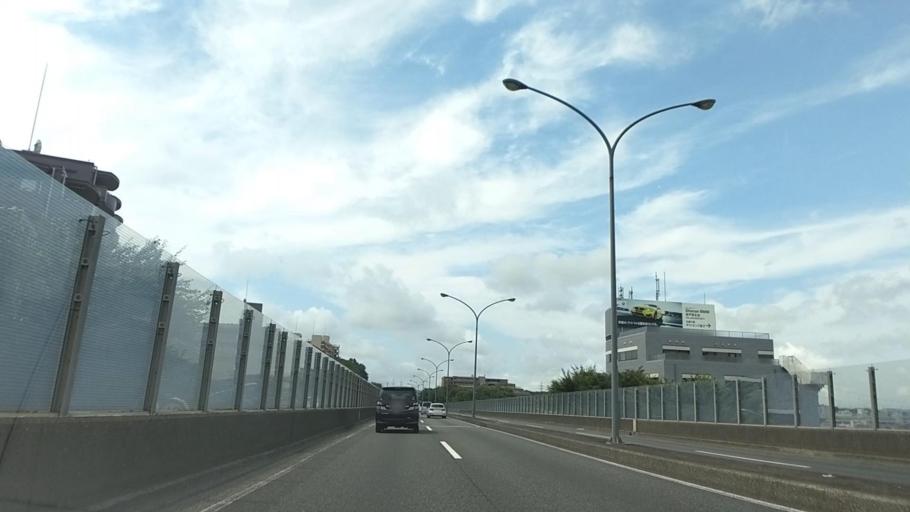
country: JP
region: Kanagawa
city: Yokohama
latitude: 35.4268
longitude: 139.5616
